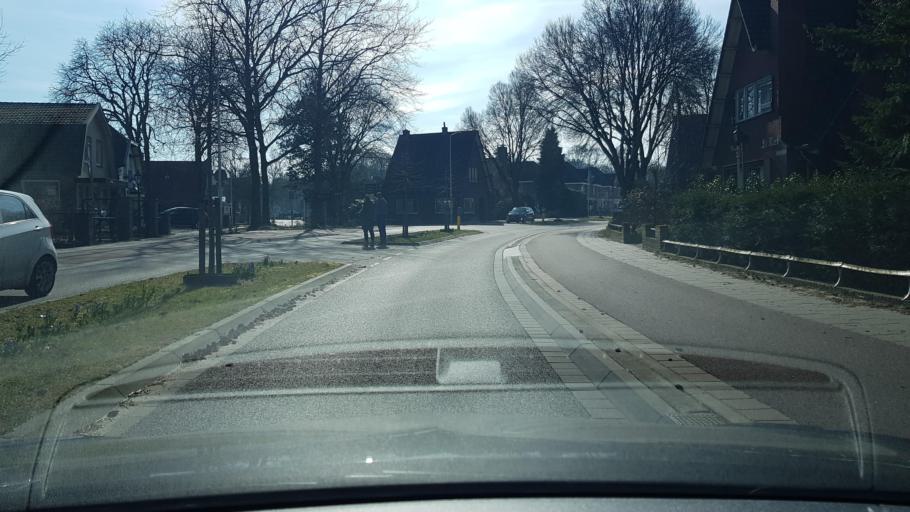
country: NL
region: Gelderland
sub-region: Gemeente Epe
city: Vaassen
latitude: 52.2851
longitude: 5.9686
